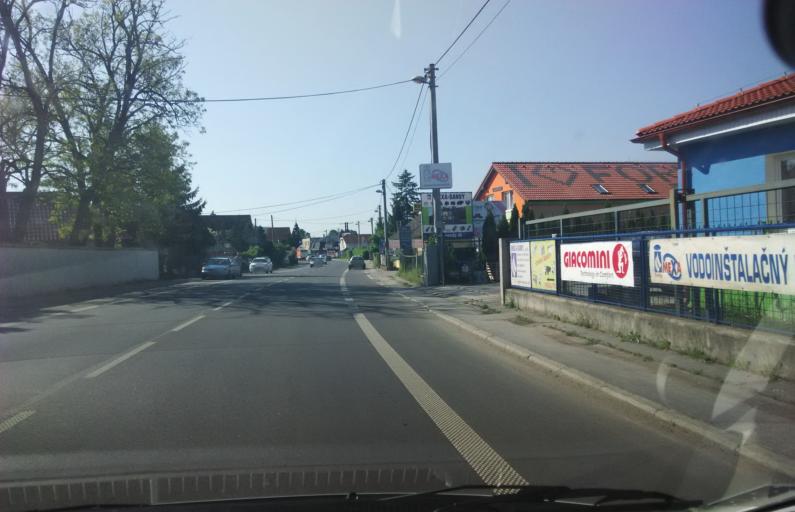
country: SK
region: Nitriansky
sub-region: Okres Nitra
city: Nitra
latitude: 48.2761
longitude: 18.0975
